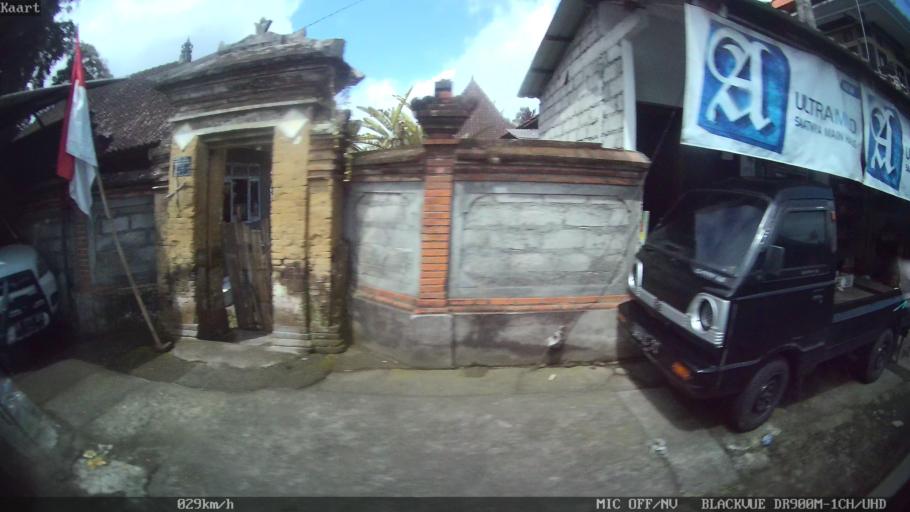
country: ID
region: Bali
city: Banjar Petak
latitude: -8.4568
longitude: 115.3204
